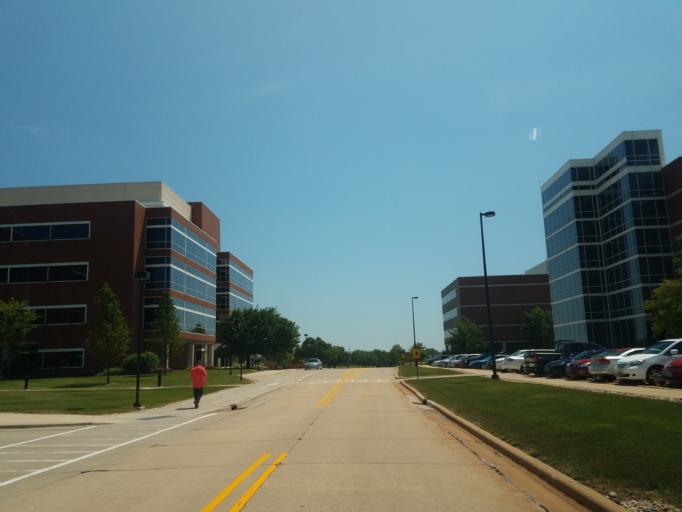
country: US
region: Illinois
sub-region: McLean County
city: Bloomington
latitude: 40.4552
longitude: -88.9545
